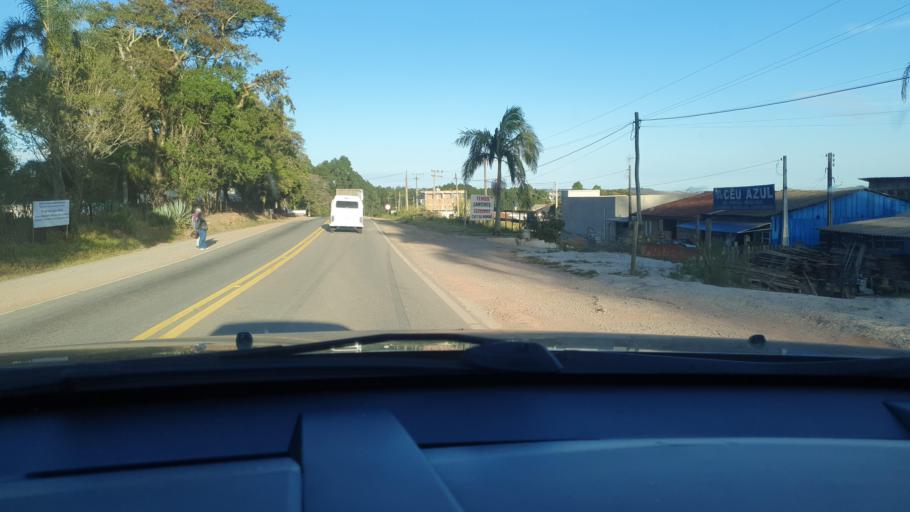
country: BR
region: Sao Paulo
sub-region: Piedade
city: Piedade
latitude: -23.7154
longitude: -47.3773
